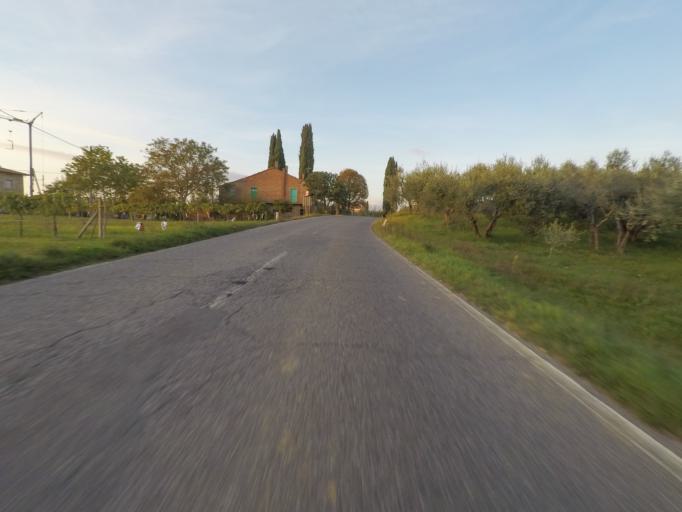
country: IT
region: Tuscany
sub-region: Provincia di Siena
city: Montepulciano
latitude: 43.1305
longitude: 11.7282
